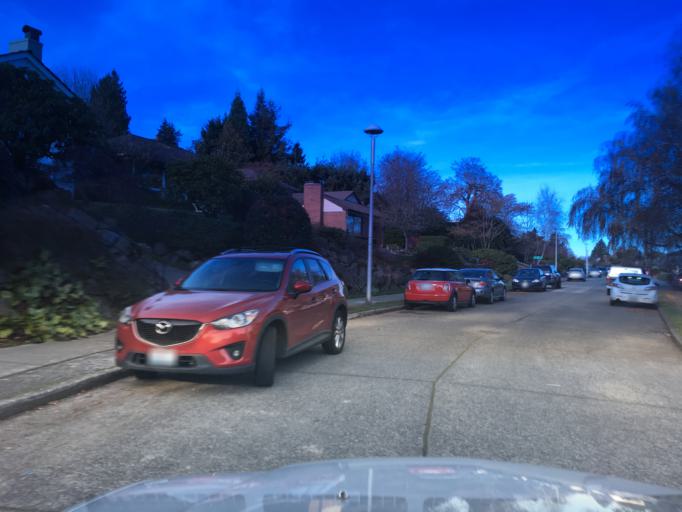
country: US
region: Washington
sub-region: King County
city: Inglewood-Finn Hill
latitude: 47.6796
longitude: -122.2660
